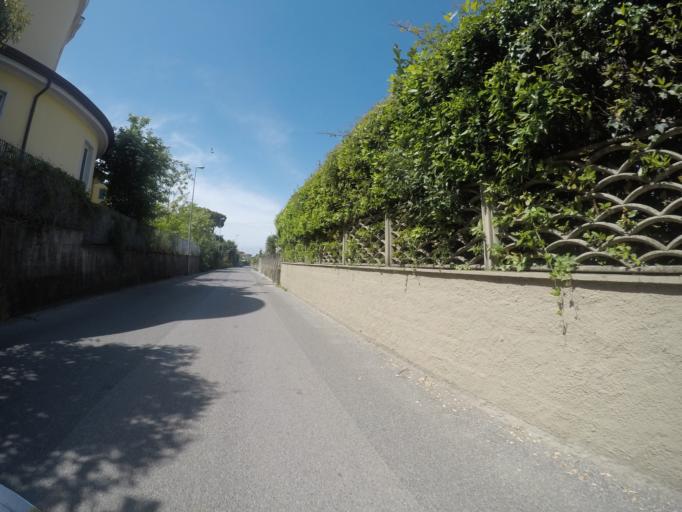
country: IT
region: Tuscany
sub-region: Provincia di Massa-Carrara
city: Massa
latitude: 44.0393
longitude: 10.1117
